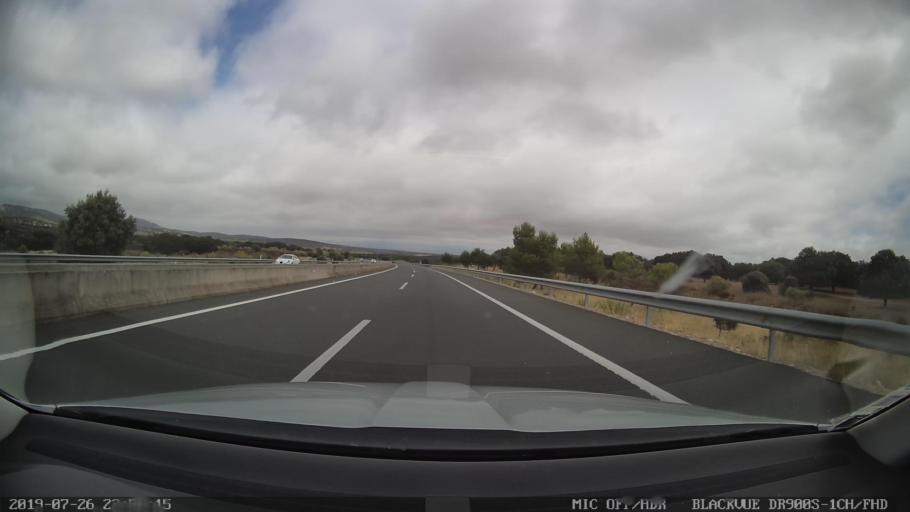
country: ES
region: Extremadura
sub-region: Provincia de Caceres
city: Casas de Miravete
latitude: 39.7648
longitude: -5.7339
